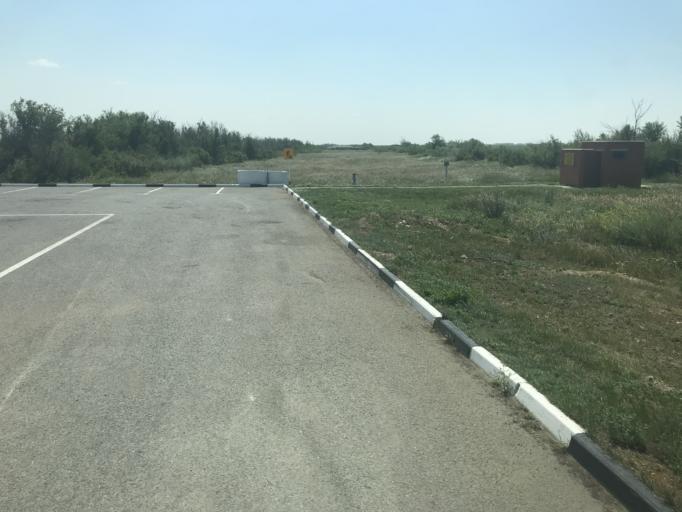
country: KZ
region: Aqmola
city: Kokshetau
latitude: 53.6355
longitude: 69.4554
